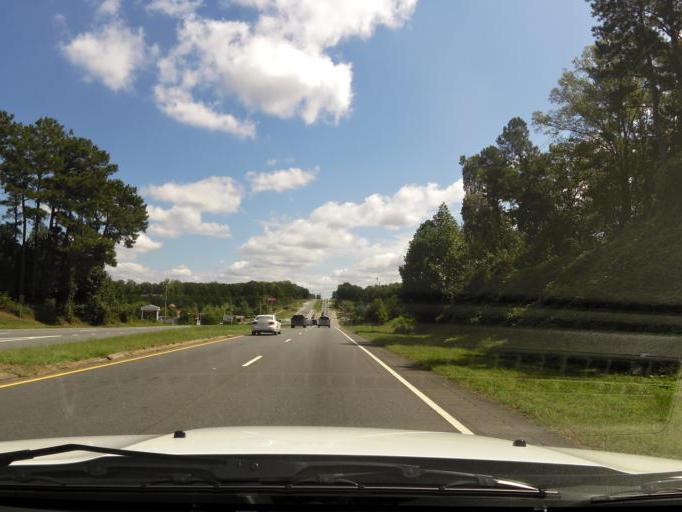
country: US
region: Georgia
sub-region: Cobb County
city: Acworth
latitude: 34.0313
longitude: -84.6608
